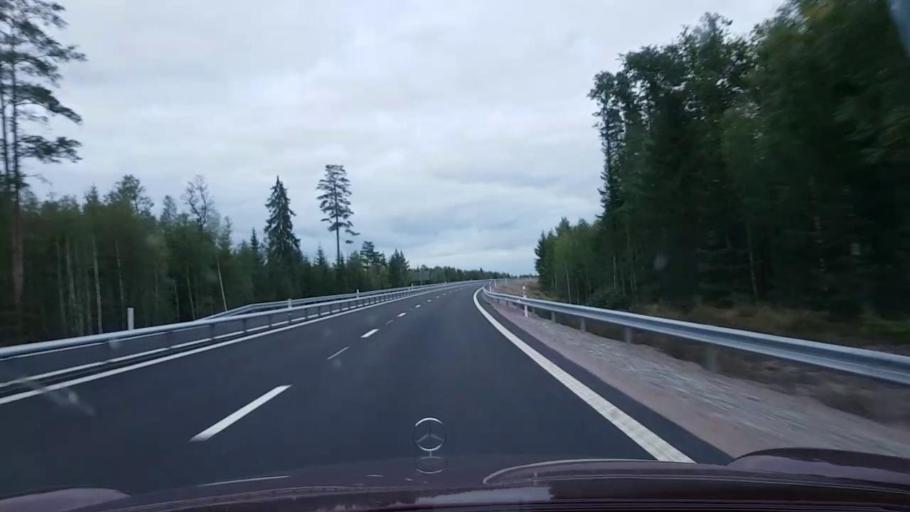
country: SE
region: Vaestmanland
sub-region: Surahammars Kommun
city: Surahammar
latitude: 59.6621
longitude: 16.2084
